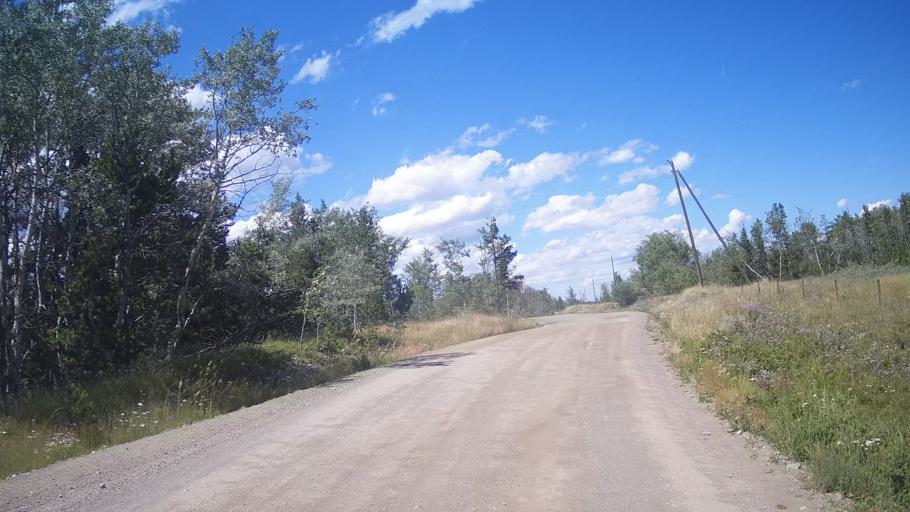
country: CA
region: British Columbia
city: Cache Creek
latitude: 51.2605
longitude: -121.6926
